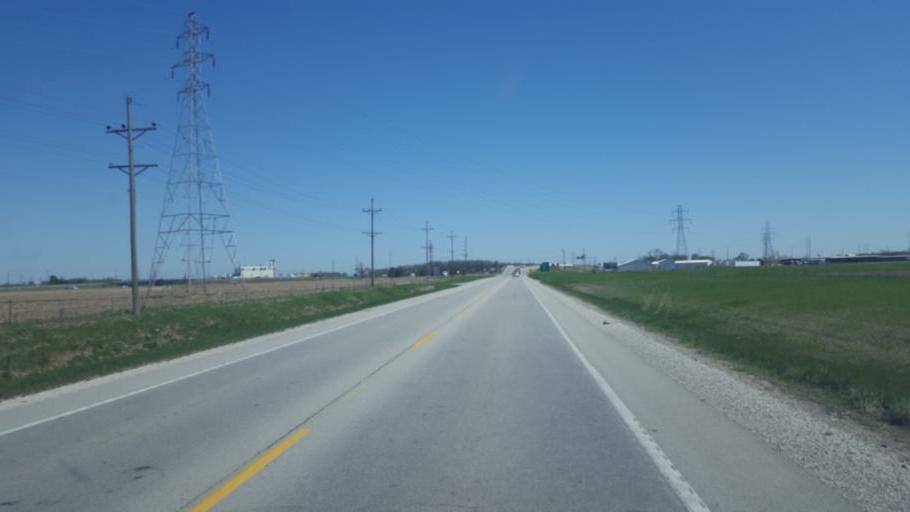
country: US
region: Ohio
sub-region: Sandusky County
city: Stony Prairie
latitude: 41.3622
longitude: -83.1639
